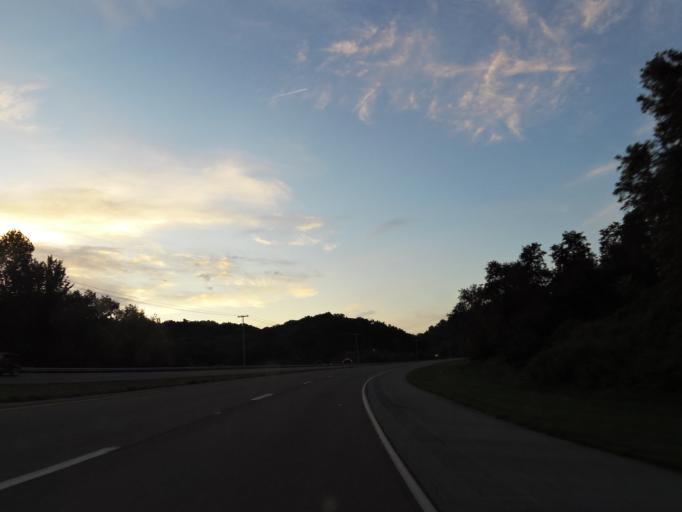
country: US
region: Tennessee
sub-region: Carter County
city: Elizabethton
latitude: 36.3632
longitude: -82.2065
